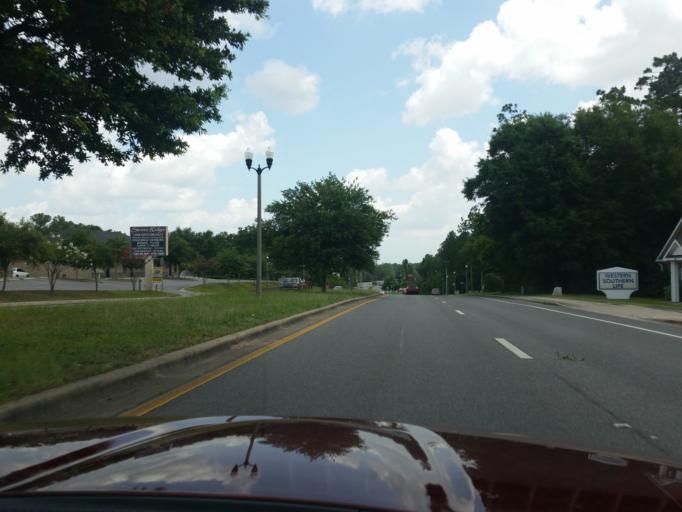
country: US
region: Florida
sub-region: Escambia County
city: Ferry Pass
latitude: 30.5265
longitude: -87.2212
